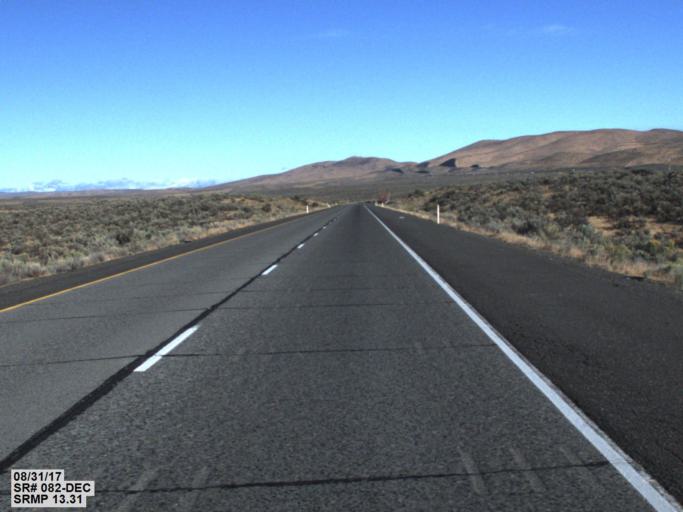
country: US
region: Washington
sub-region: Kittitas County
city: Kittitas
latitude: 46.8232
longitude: -120.3602
